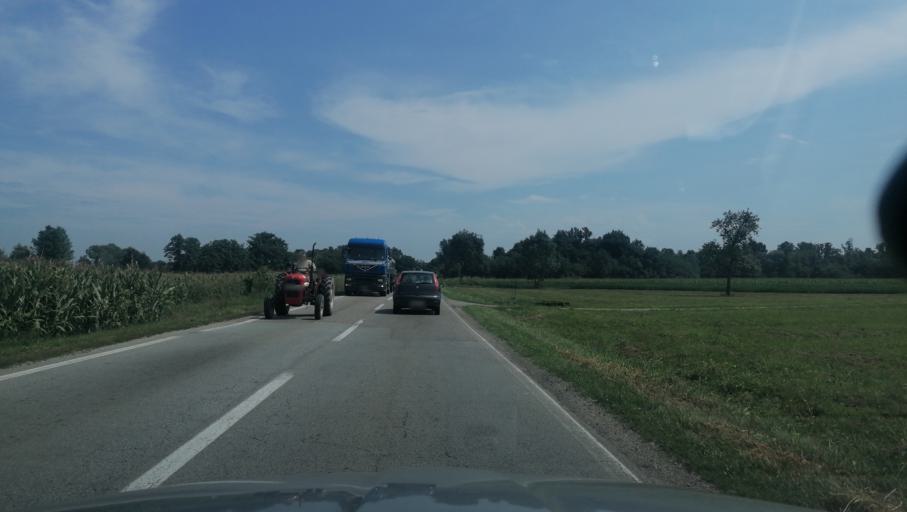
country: BA
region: Republika Srpska
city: Velika Obarska
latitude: 44.8254
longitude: 19.0384
